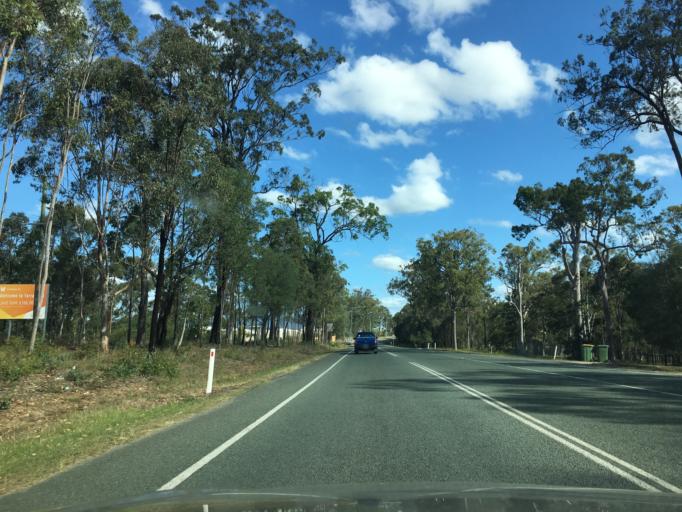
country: AU
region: Queensland
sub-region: Logan
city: Chambers Flat
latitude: -27.7946
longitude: 153.0995
